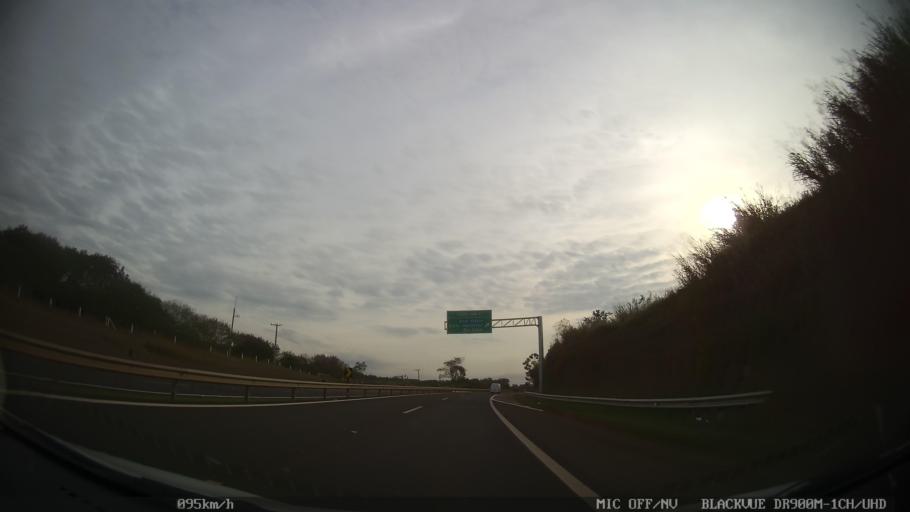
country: BR
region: Sao Paulo
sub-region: Piracicaba
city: Piracicaba
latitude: -22.7004
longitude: -47.5993
